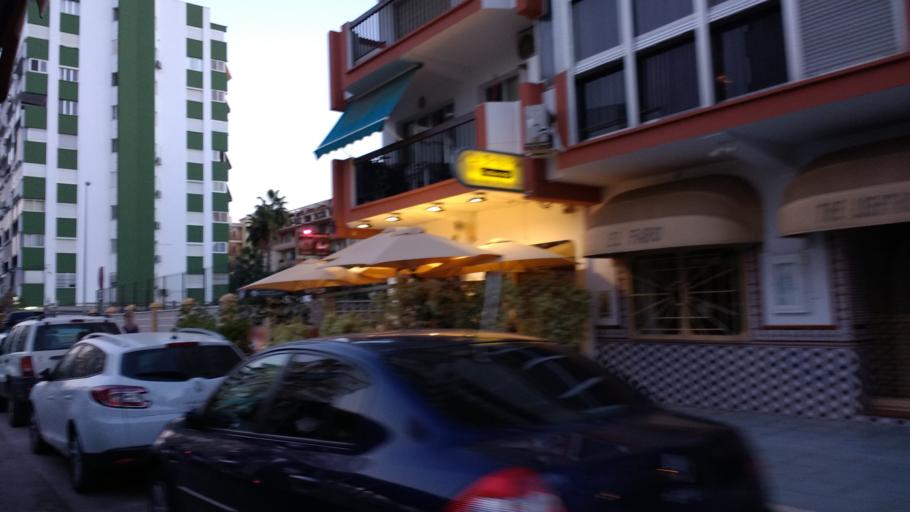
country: ES
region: Andalusia
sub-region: Provincia de Malaga
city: Velez-Malaga
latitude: 36.7375
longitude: -4.0985
